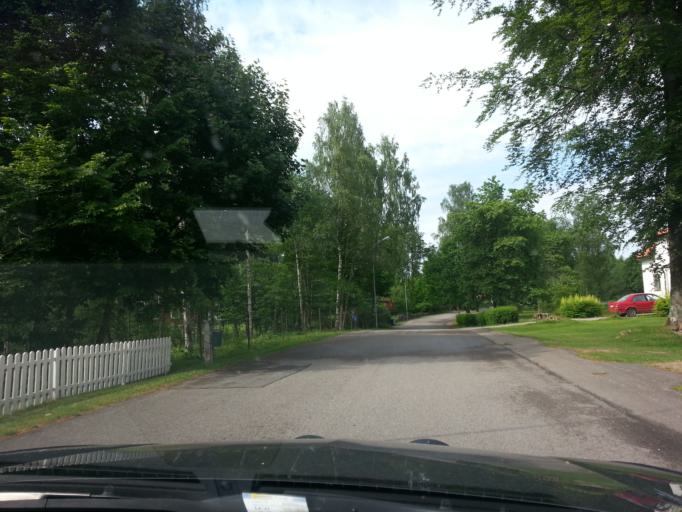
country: SE
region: Joenkoeping
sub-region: Vetlanda Kommun
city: Vetlanda
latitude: 57.3116
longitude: 15.1209
